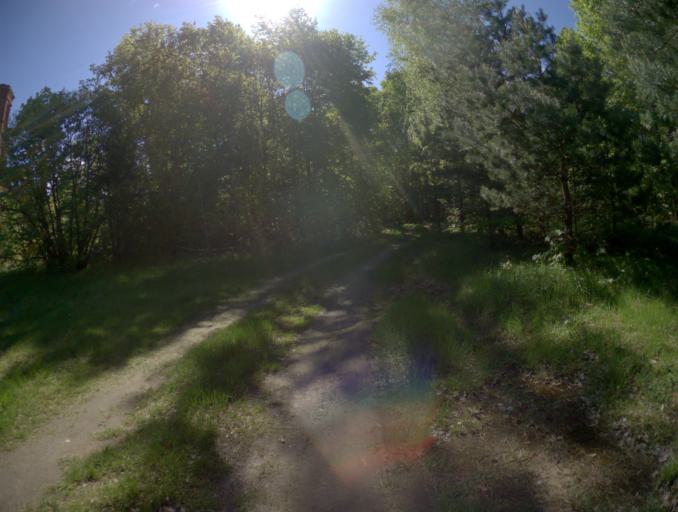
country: RU
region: Rjazan
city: Spas-Klepiki
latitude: 55.2533
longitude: 40.1125
